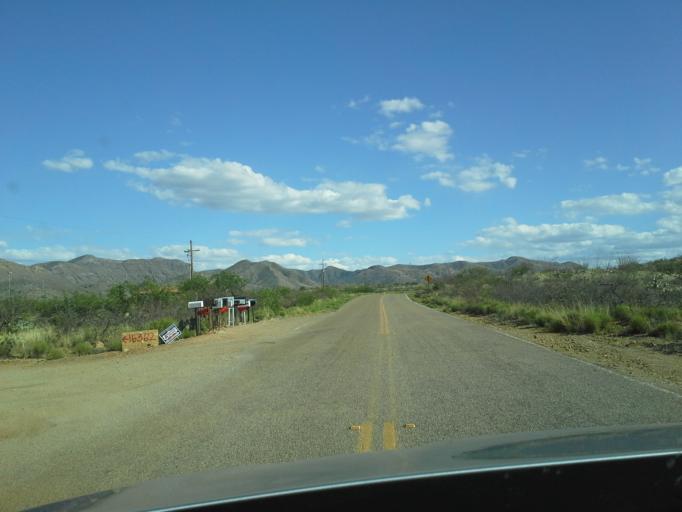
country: US
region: Arizona
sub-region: Pima County
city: Vail
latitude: 31.9509
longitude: -110.6554
